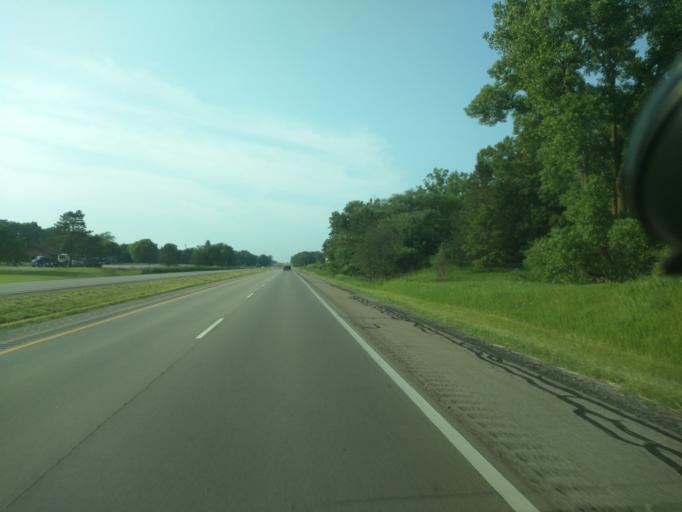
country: US
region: Michigan
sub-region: Ingham County
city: Leslie
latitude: 42.3628
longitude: -84.4288
